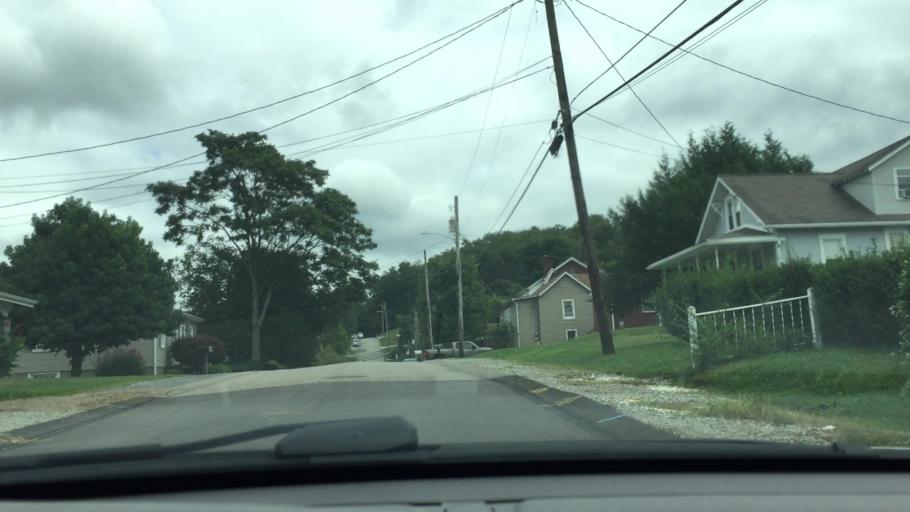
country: US
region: Pennsylvania
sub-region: Washington County
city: Houston
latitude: 40.2515
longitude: -80.1995
